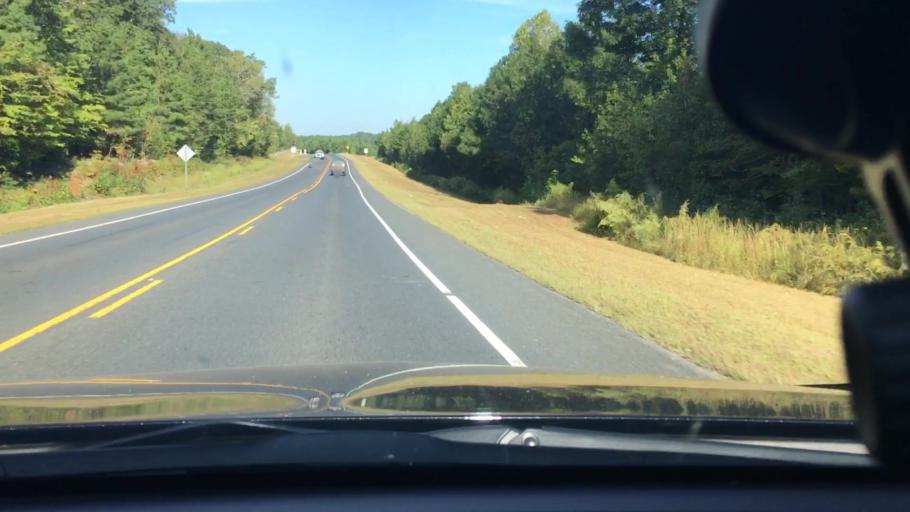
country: US
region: North Carolina
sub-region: Stanly County
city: Albemarle
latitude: 35.3822
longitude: -80.1774
